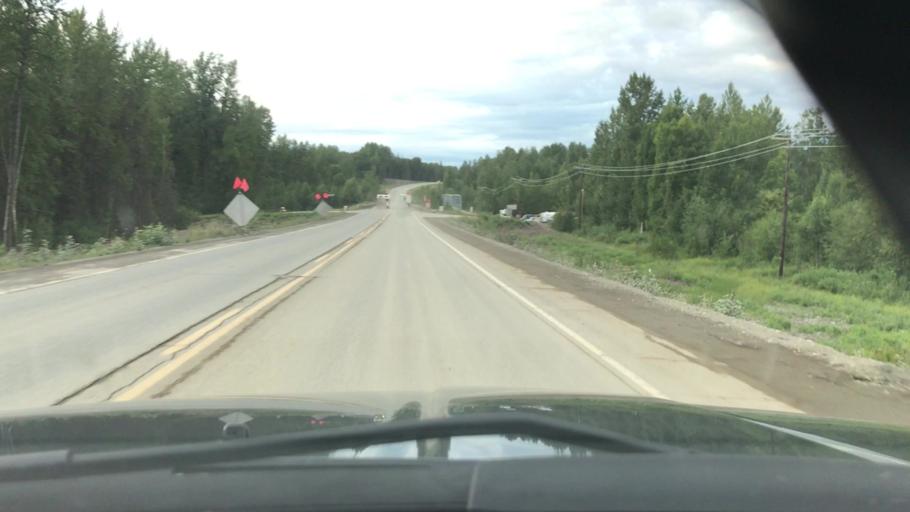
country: US
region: Alaska
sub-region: Matanuska-Susitna Borough
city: Y
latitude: 62.1018
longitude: -150.0605
